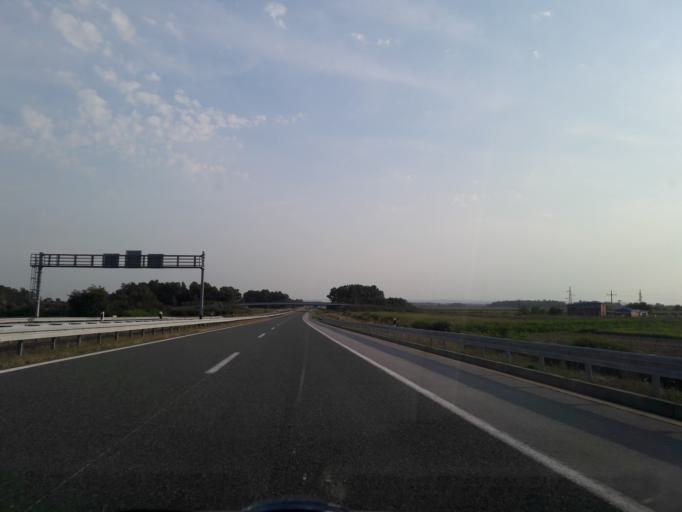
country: HR
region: Brodsko-Posavska
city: Vrpolje
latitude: 45.1989
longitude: 18.3325
